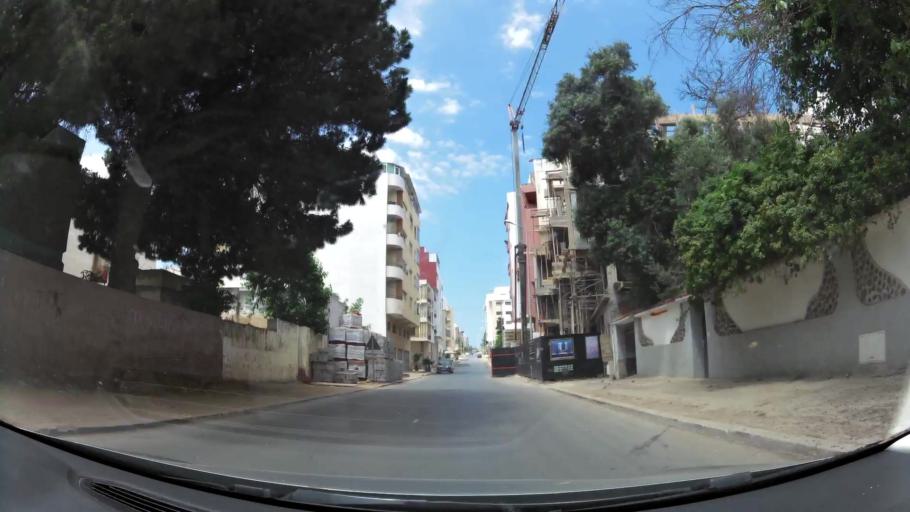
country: MA
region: Gharb-Chrarda-Beni Hssen
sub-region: Kenitra Province
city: Kenitra
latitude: 34.2631
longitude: -6.5913
